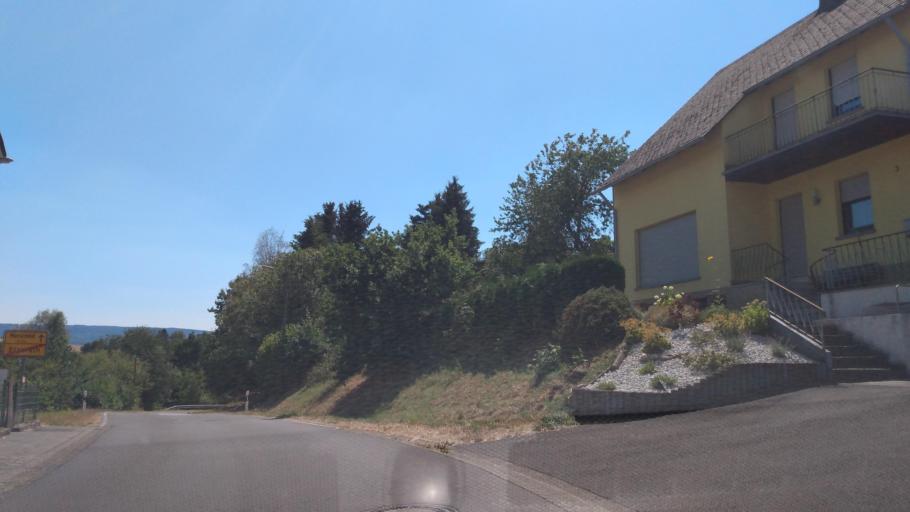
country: DE
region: Rheinland-Pfalz
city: Gornhausen
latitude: 49.8347
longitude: 7.0774
